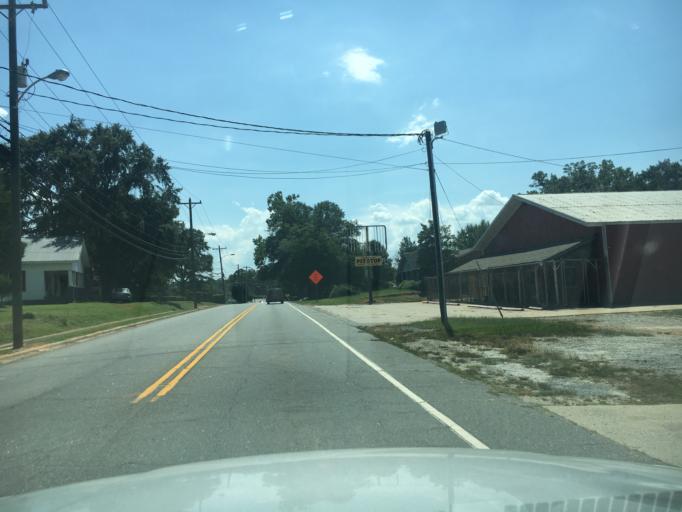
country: US
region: North Carolina
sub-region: Rutherford County
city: Forest City
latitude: 35.3110
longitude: -81.8579
